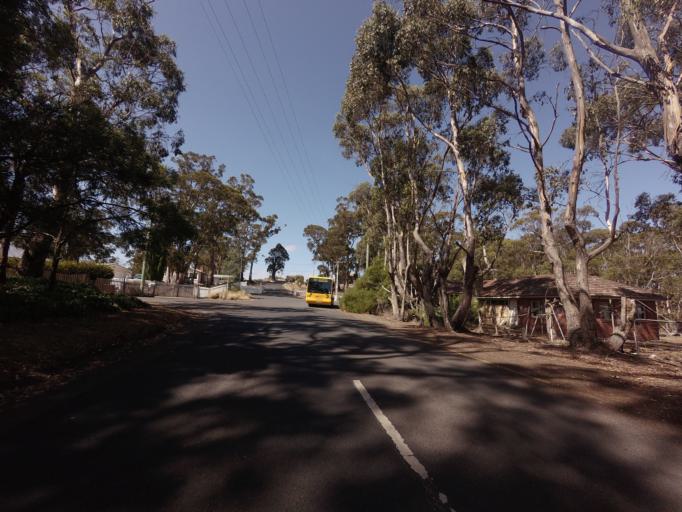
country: AU
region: Tasmania
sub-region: Kingborough
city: Taroona
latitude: -42.9246
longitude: 147.3423
